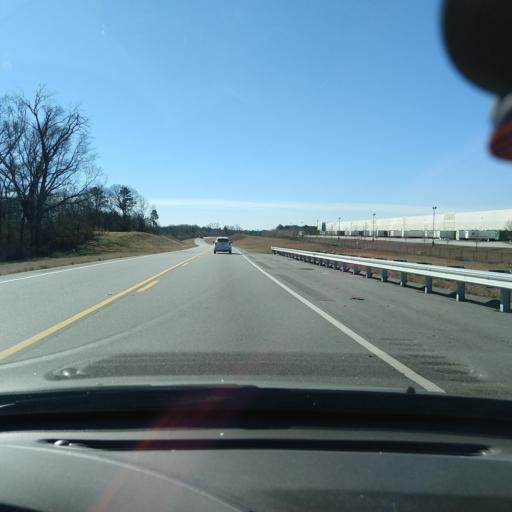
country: US
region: Georgia
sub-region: Walton County
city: Social Circle
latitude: 33.6494
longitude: -83.6908
